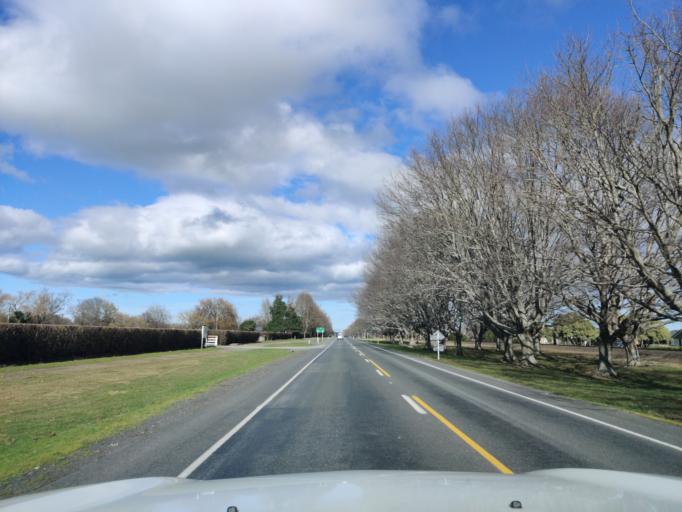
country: NZ
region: Waikato
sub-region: Matamata-Piako District
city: Matamata
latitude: -37.8276
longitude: 175.7696
